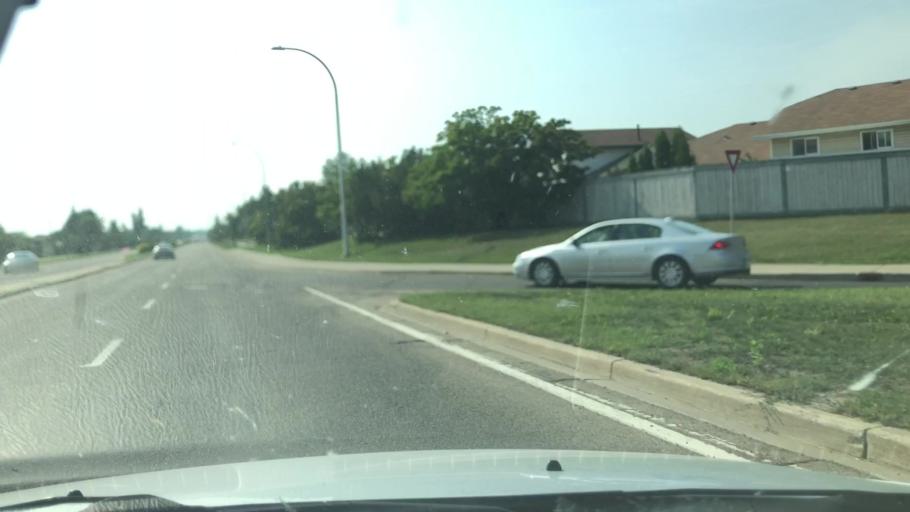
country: CA
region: Alberta
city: Edmonton
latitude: 53.6159
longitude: -113.4430
